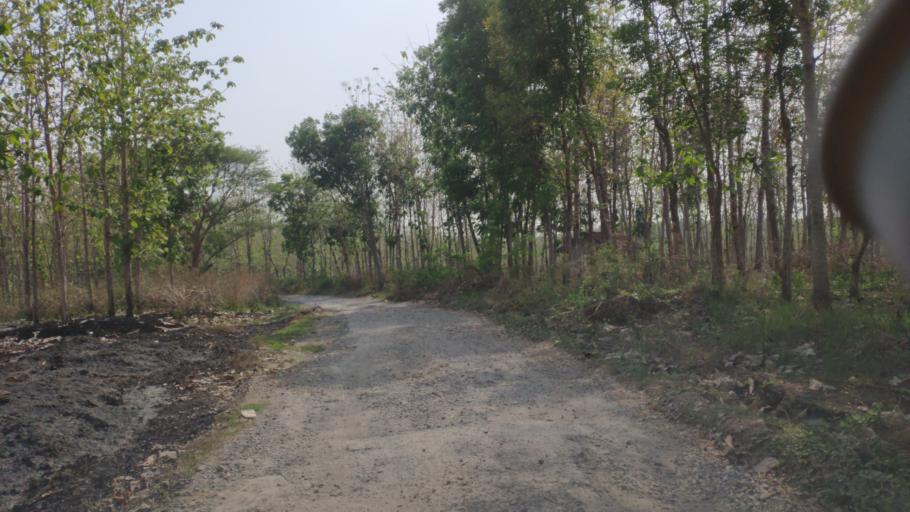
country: ID
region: Central Java
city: Randublatung
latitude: -7.2649
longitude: 111.2723
